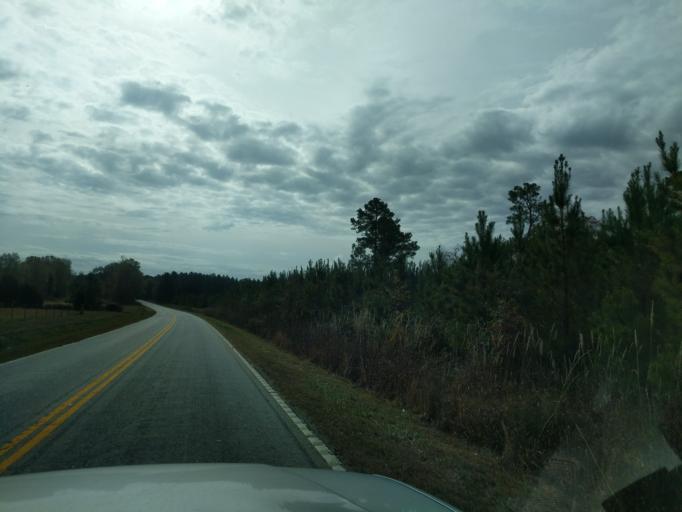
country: US
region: South Carolina
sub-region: Laurens County
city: Joanna
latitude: 34.3629
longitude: -81.8611
